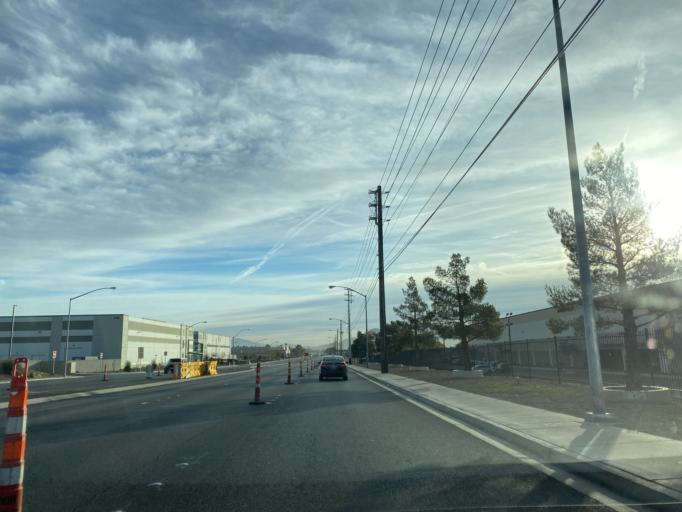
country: US
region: Nevada
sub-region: Clark County
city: Nellis Air Force Base
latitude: 36.2403
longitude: -115.0773
